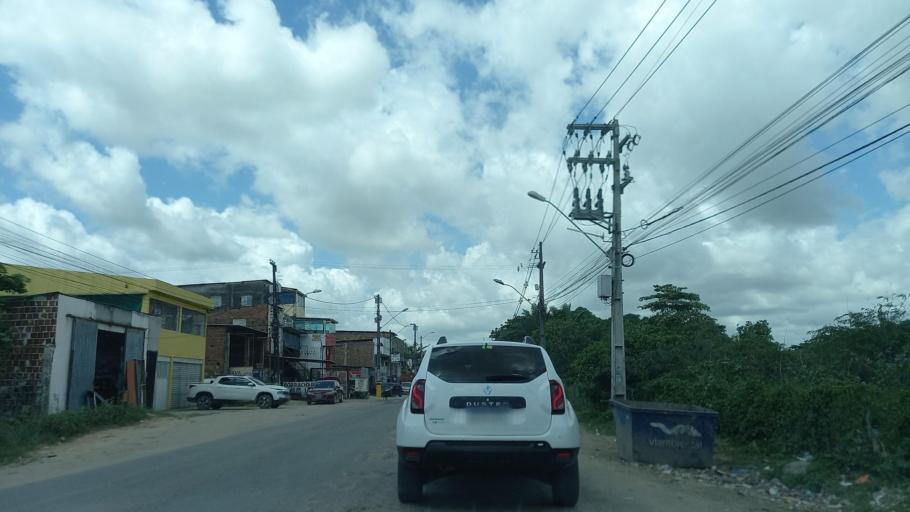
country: BR
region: Pernambuco
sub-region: Jaboatao Dos Guararapes
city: Jaboatao
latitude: -8.1574
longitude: -34.9703
